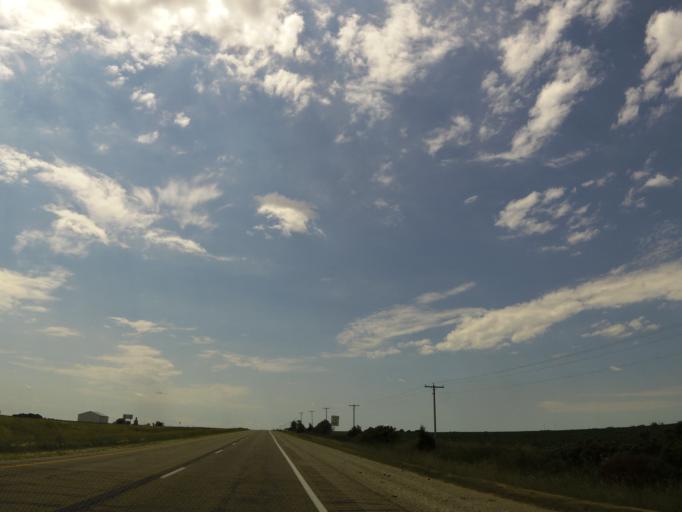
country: US
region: Iowa
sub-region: Bremer County
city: Tripoli
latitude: 42.7734
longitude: -92.3374
